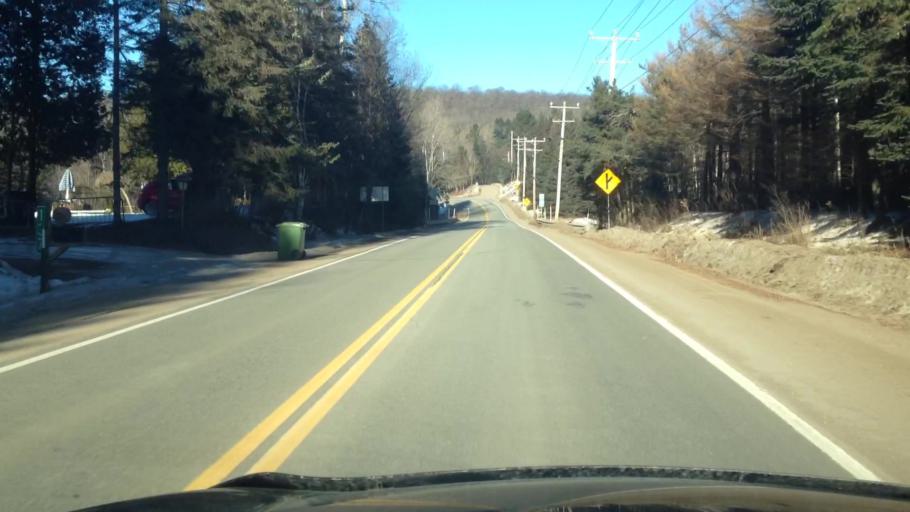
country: CA
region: Quebec
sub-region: Laurentides
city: Mont-Tremblant
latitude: 45.9855
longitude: -74.6112
